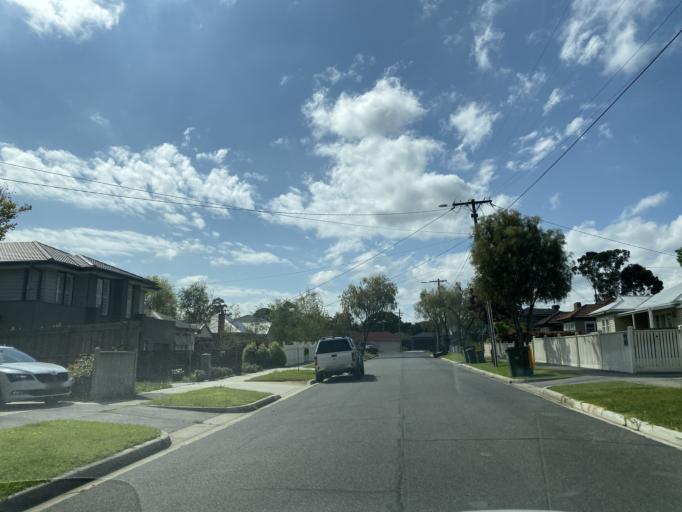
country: AU
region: Victoria
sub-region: Whitehorse
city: Burwood
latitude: -37.8458
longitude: 145.1265
